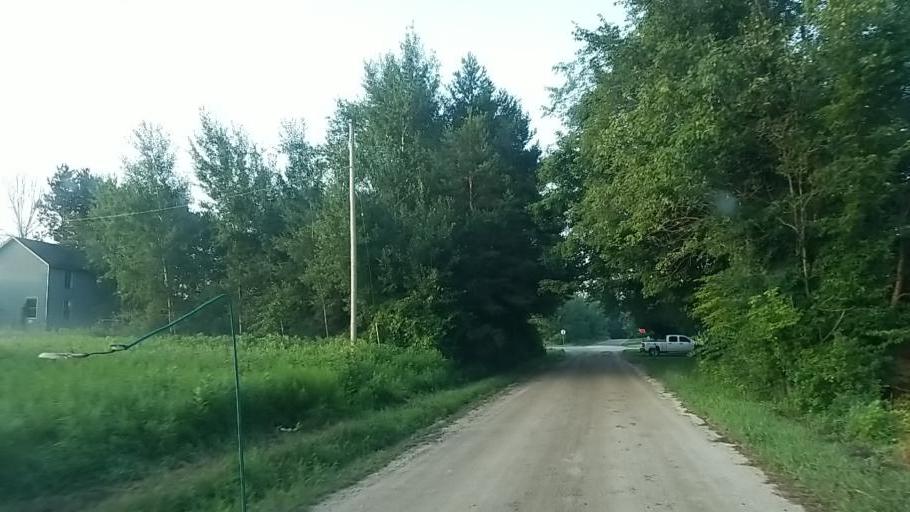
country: US
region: Michigan
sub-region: Osceola County
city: Evart
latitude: 43.9017
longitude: -85.1676
